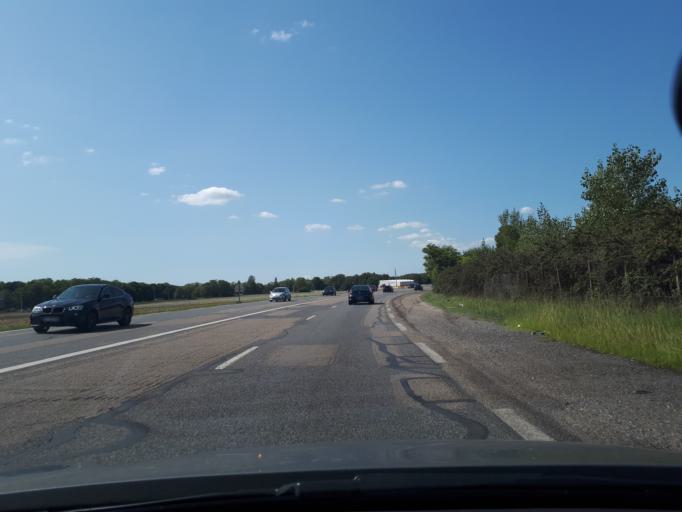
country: FR
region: Rhone-Alpes
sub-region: Departement du Rhone
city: Saint-Priest
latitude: 45.7182
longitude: 4.9438
